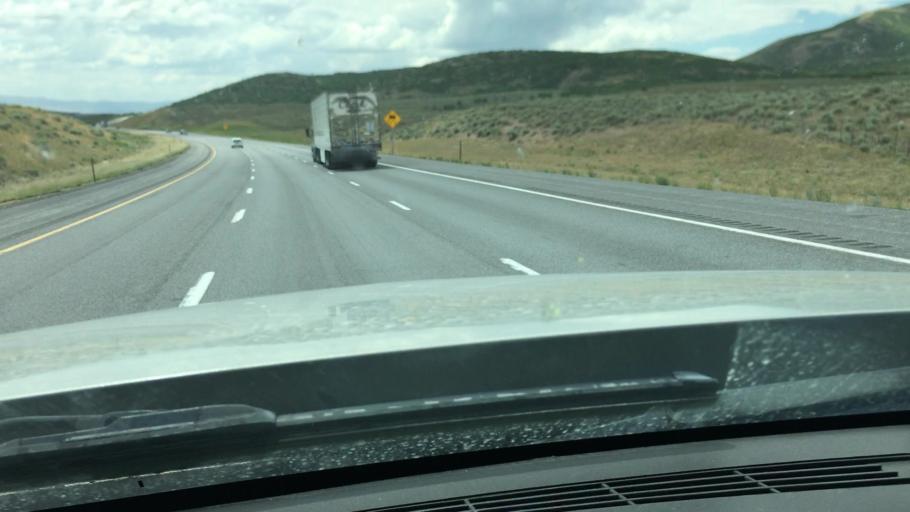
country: US
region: Utah
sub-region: Beaver County
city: Beaver
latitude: 38.4669
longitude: -112.6180
